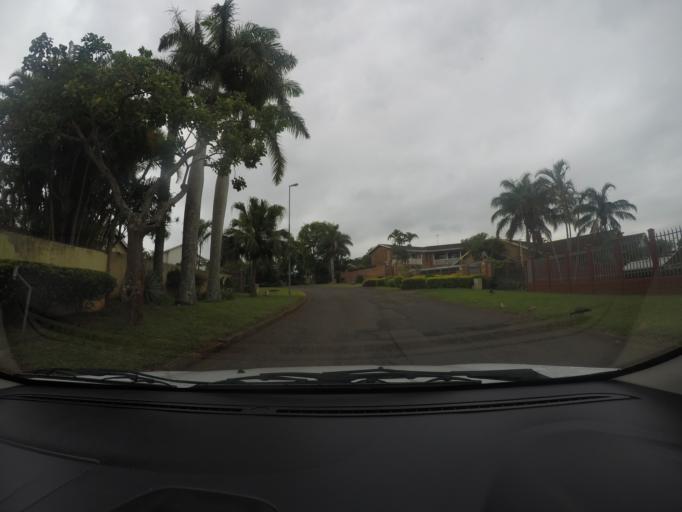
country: ZA
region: KwaZulu-Natal
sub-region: uThungulu District Municipality
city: Empangeni
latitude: -28.7652
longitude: 31.8915
